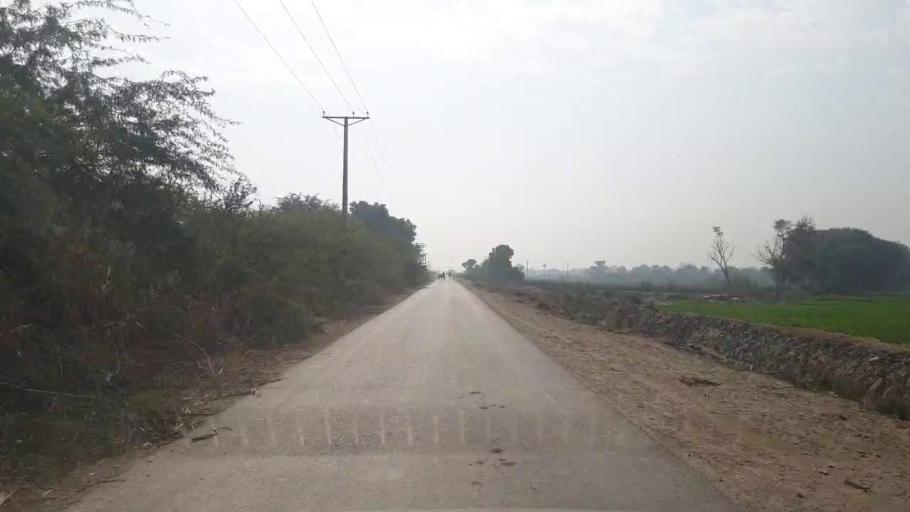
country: PK
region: Sindh
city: Hala
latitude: 25.7815
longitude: 68.4429
